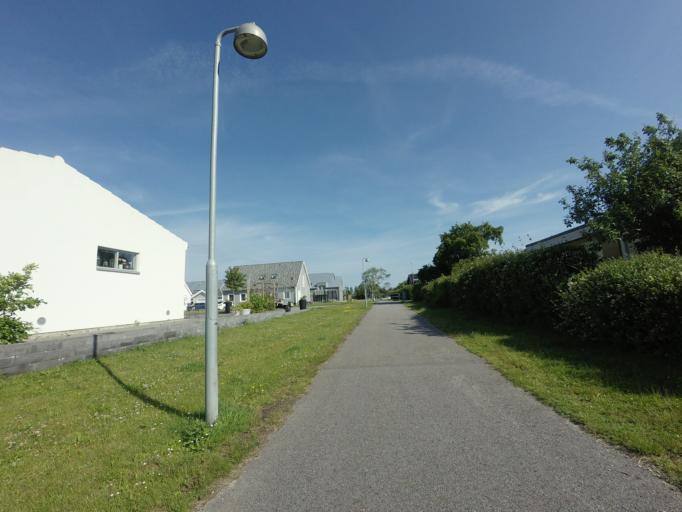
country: SE
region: Skane
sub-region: Malmo
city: Oxie
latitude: 55.4922
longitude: 13.1071
